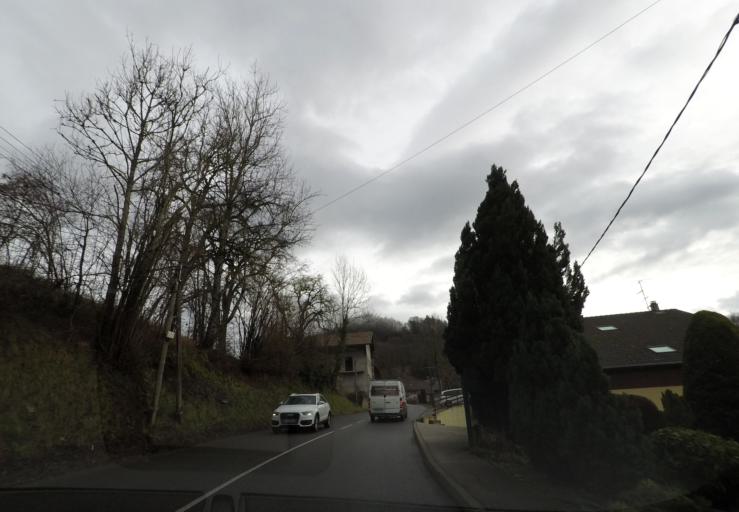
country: FR
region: Rhone-Alpes
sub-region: Departement de la Haute-Savoie
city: Chatillon-sur-Cluses
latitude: 46.0861
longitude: 6.5793
